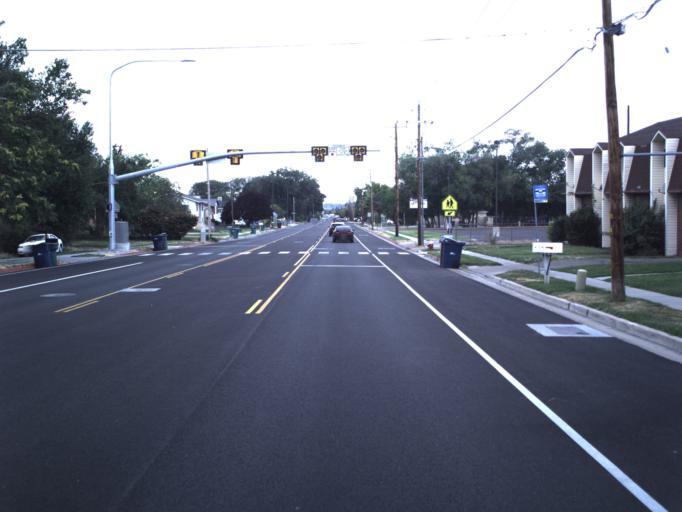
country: US
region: Utah
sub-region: Weber County
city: Roy
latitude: 41.1617
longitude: -112.0482
